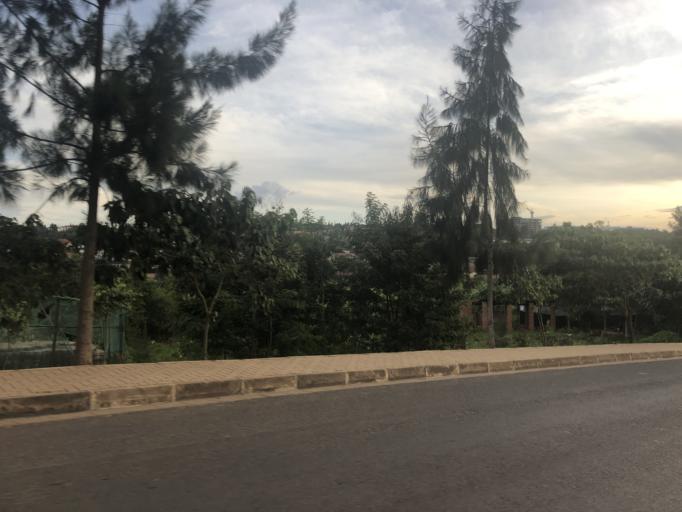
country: RW
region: Kigali
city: Kigali
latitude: -1.9316
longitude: 30.0898
